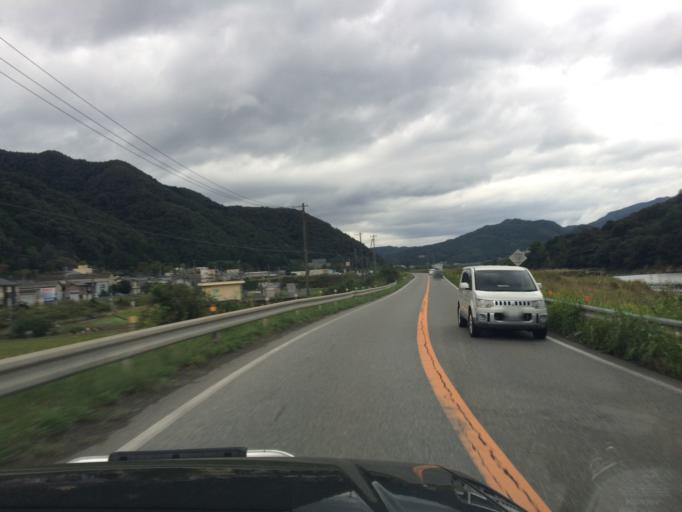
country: JP
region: Hyogo
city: Toyooka
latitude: 35.4103
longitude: 134.7789
